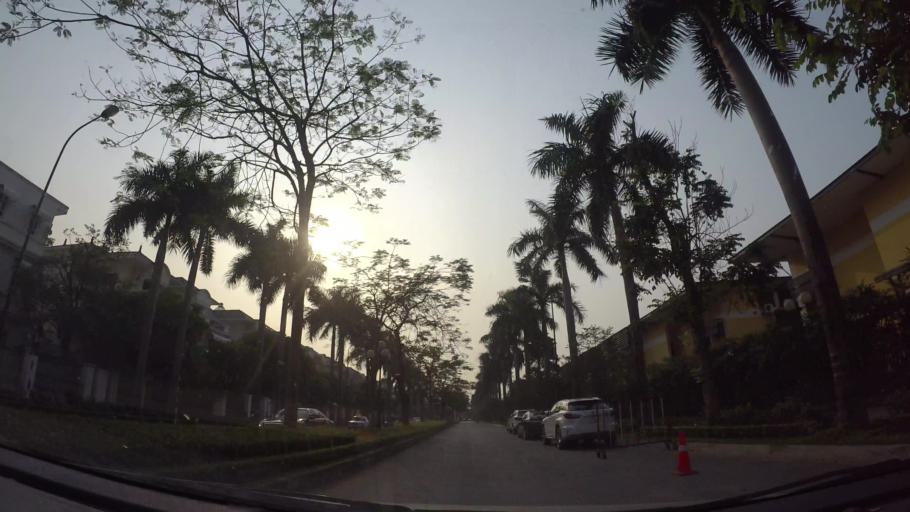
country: VN
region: Ha Noi
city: Tay Ho
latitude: 21.0742
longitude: 105.8075
